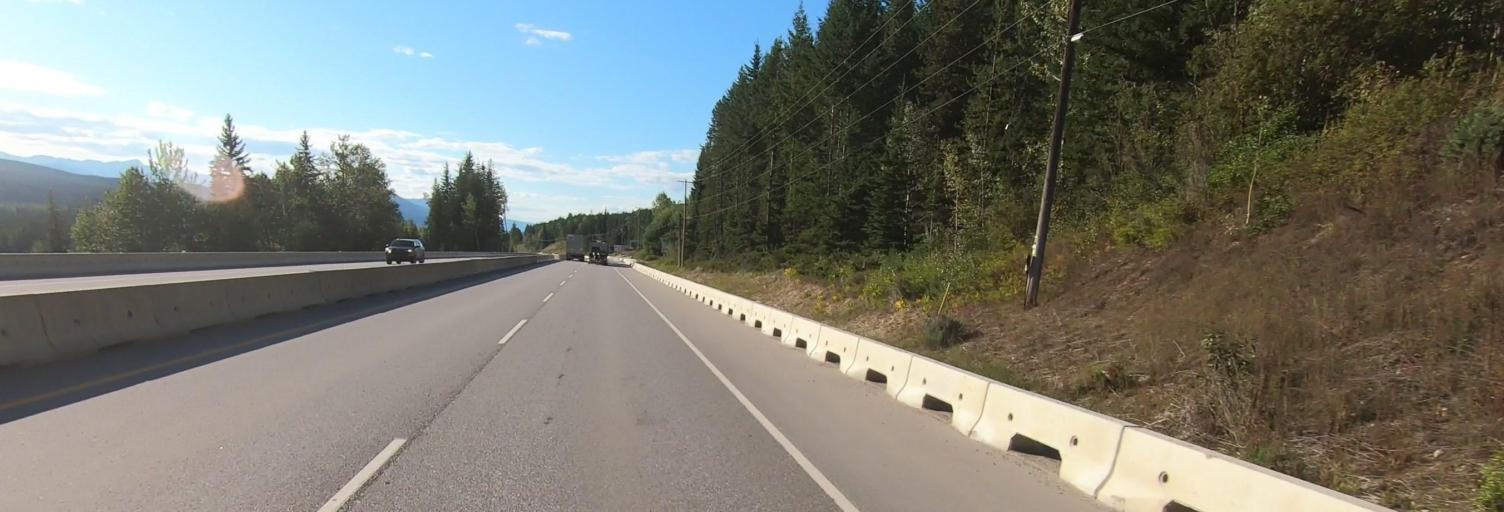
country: CA
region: British Columbia
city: Golden
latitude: 51.4664
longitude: -117.1249
